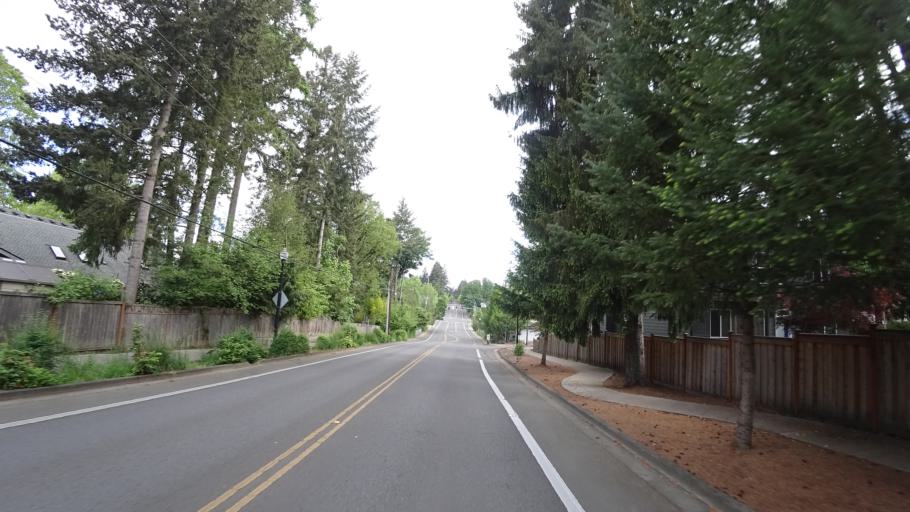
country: US
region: Oregon
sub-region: Washington County
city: Beaverton
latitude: 45.4639
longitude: -122.8363
